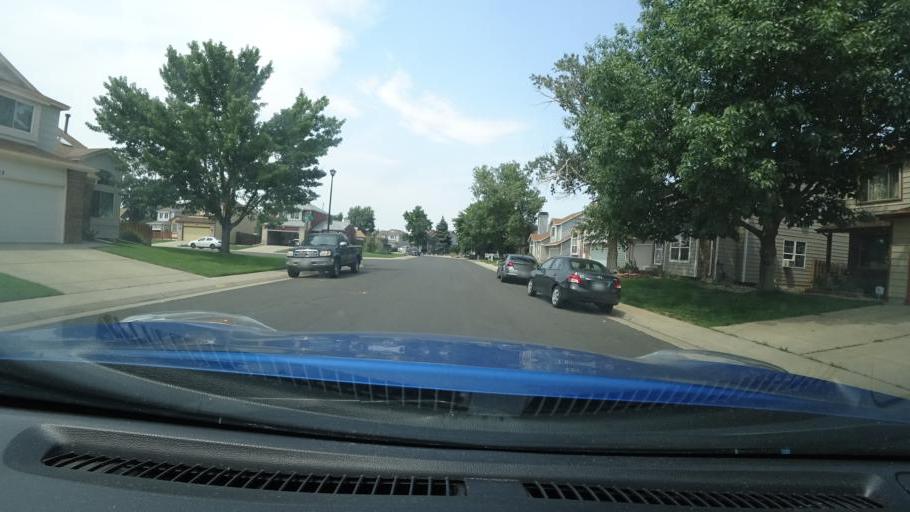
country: US
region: Colorado
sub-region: Adams County
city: Aurora
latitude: 39.7771
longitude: -104.7433
